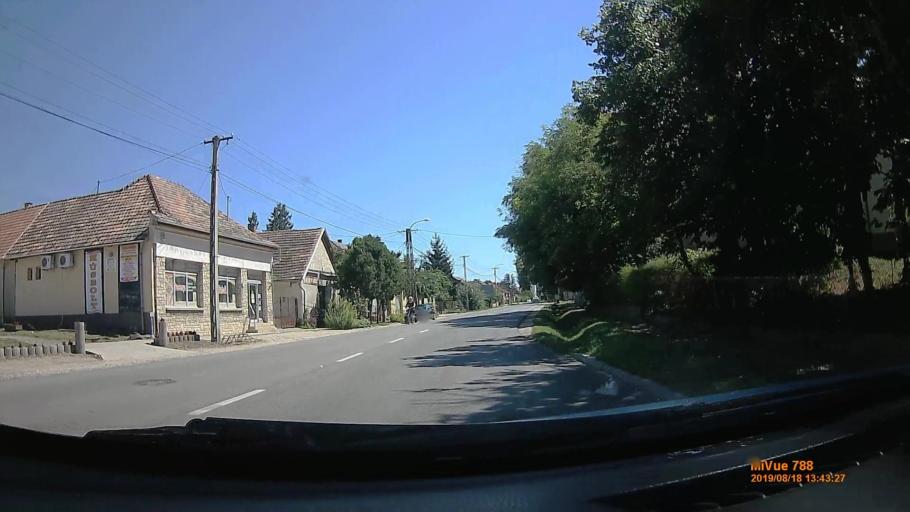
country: HU
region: Fejer
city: Cece
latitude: 46.7697
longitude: 18.6284
